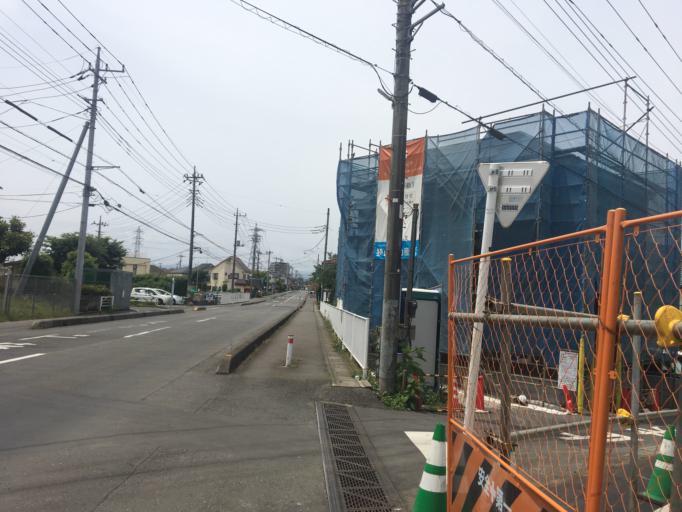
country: JP
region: Saitama
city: Sayama
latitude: 35.8341
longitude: 139.4055
